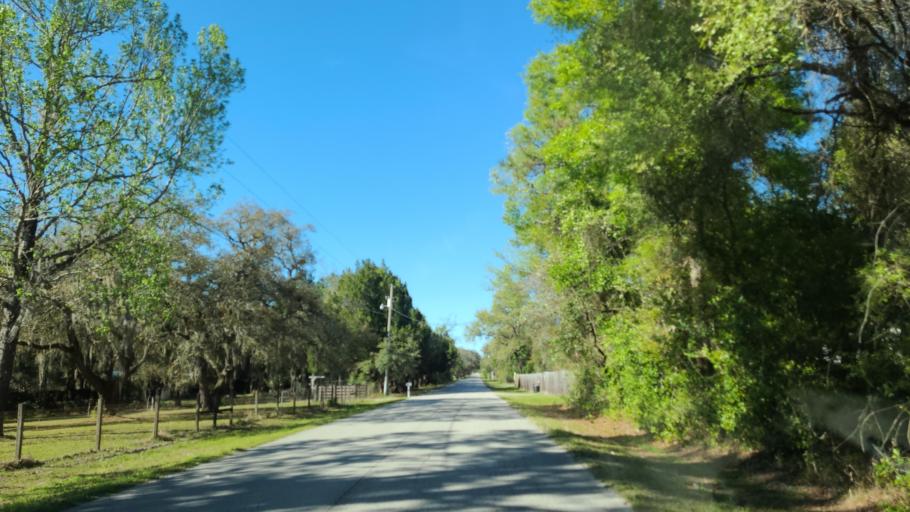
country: US
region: Florida
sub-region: Pasco County
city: Shady Hills
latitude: 28.4034
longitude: -82.5737
